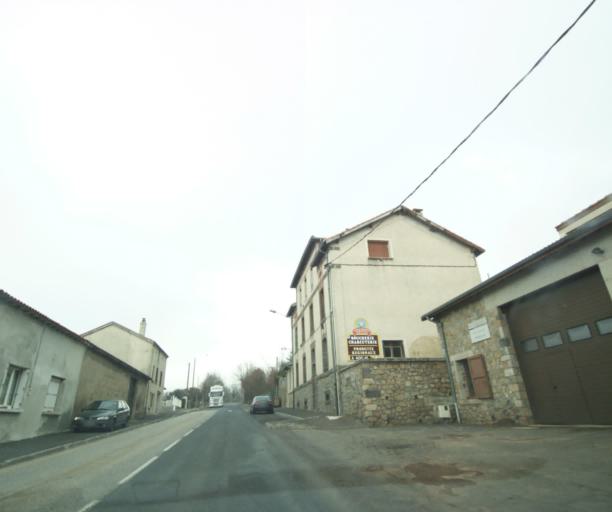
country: FR
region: Languedoc-Roussillon
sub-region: Departement de la Lozere
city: Langogne
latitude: 44.7723
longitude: 3.8840
